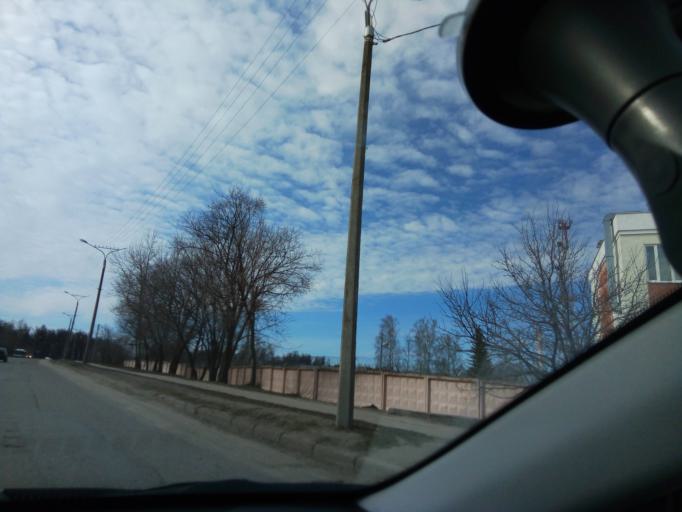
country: RU
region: Chuvashia
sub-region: Cheboksarskiy Rayon
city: Cheboksary
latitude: 56.0952
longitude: 47.2641
